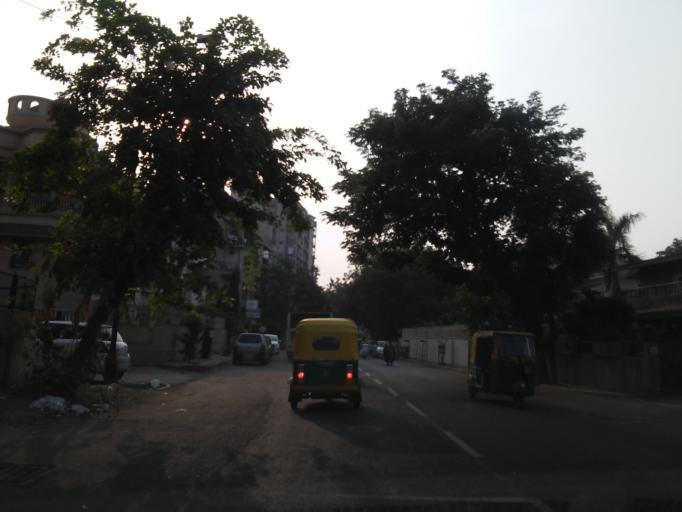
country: IN
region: Gujarat
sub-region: Ahmadabad
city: Ahmedabad
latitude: 23.0095
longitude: 72.5504
